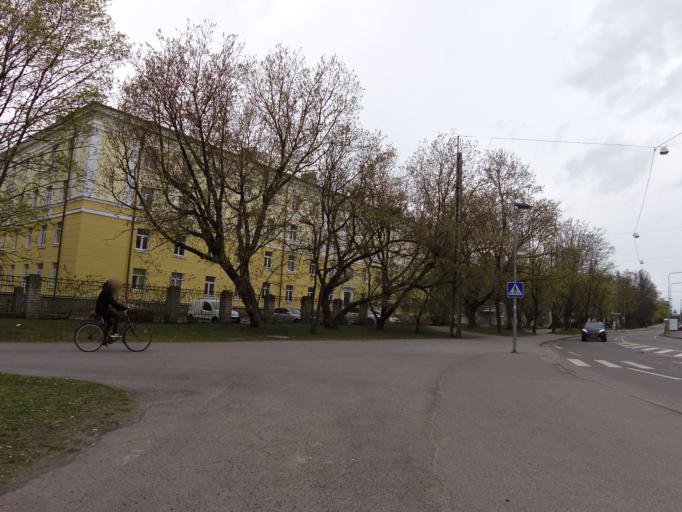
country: EE
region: Harju
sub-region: Tallinna linn
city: Tallinn
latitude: 59.4546
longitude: 24.6822
